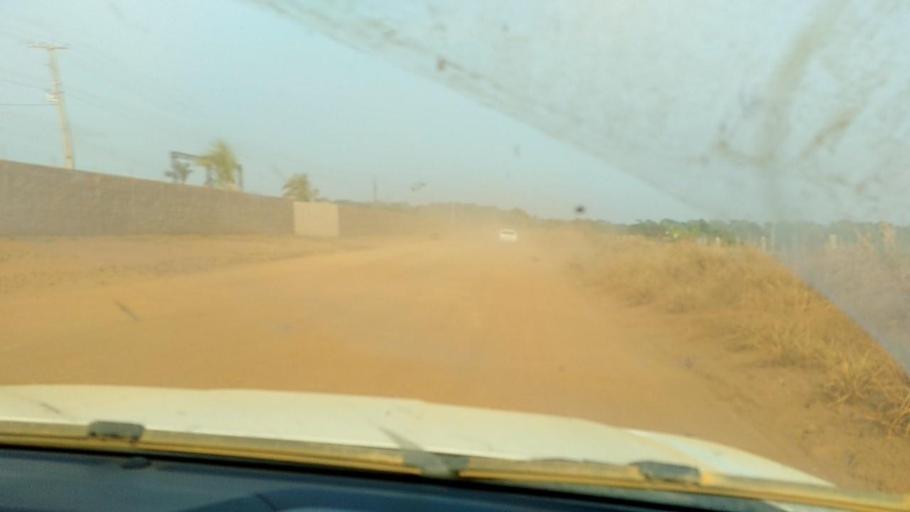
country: BR
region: Rondonia
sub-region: Porto Velho
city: Porto Velho
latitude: -8.7596
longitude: -63.9737
